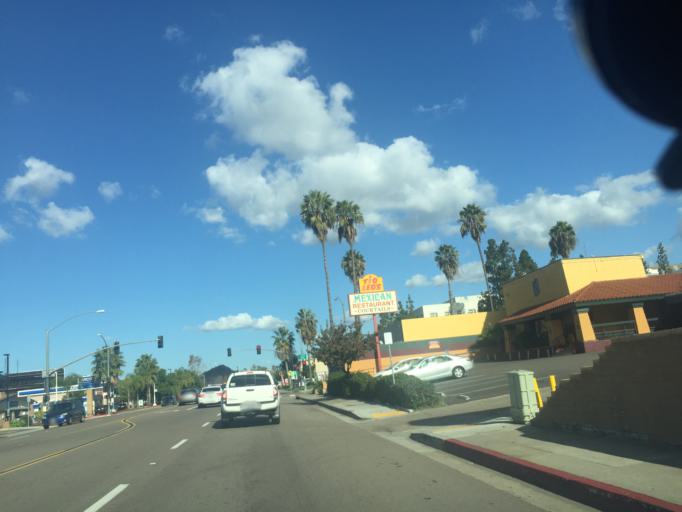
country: US
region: California
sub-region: San Diego County
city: La Mesa
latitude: 32.7891
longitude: -117.0977
